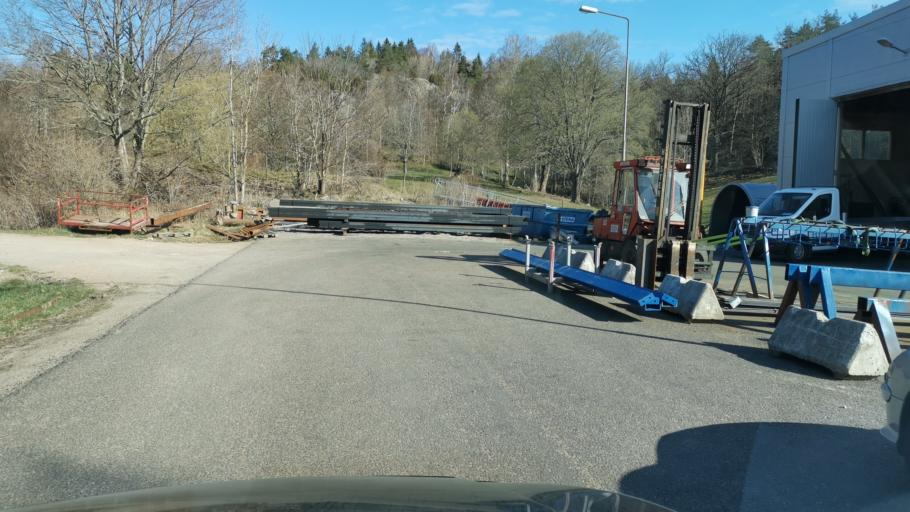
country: SE
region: Vaestra Goetaland
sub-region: Uddevalla Kommun
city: Uddevalla
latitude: 58.3594
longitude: 11.9763
